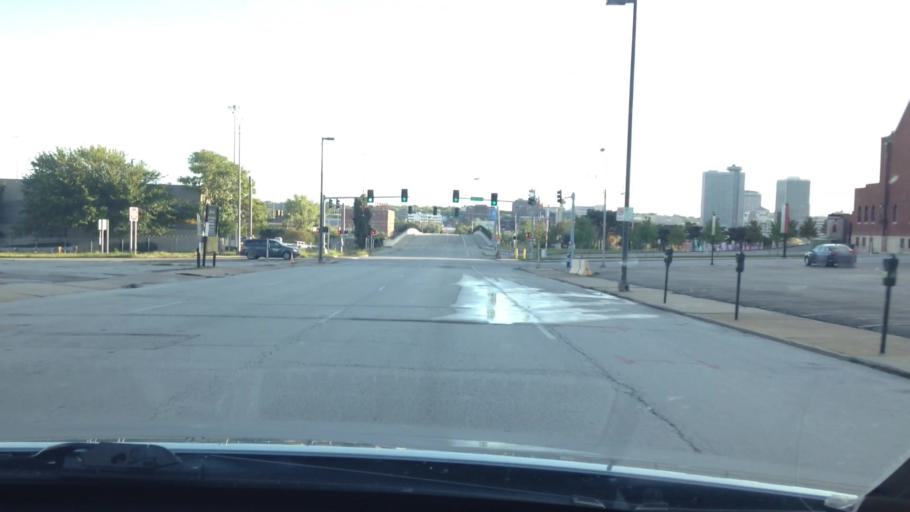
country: US
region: Missouri
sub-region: Jackson County
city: Kansas City
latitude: 39.0990
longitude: -94.5740
